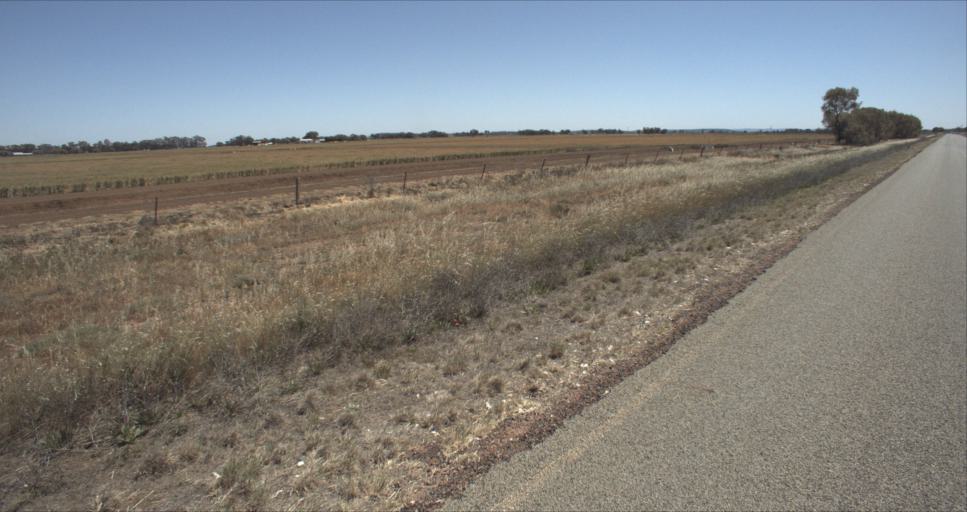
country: AU
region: New South Wales
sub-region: Leeton
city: Leeton
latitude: -34.4623
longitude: 146.2939
